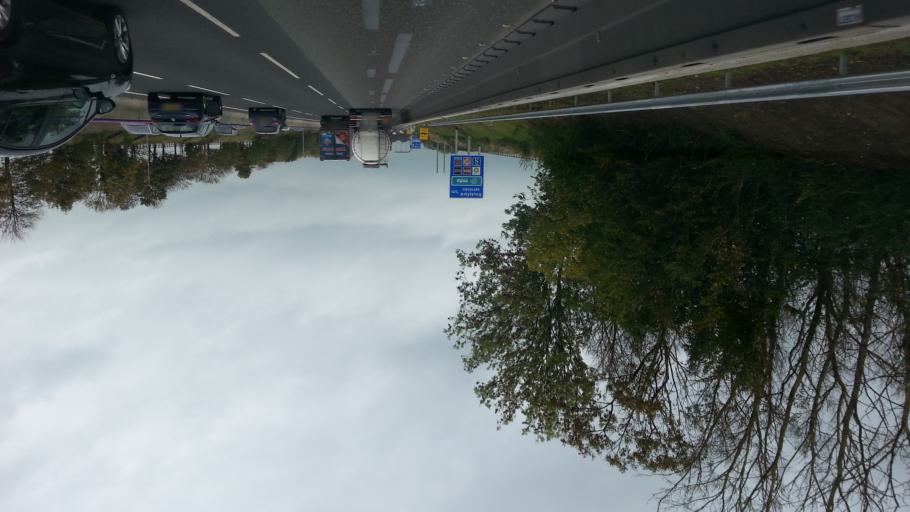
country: GB
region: England
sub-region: Cheshire East
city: Knutsford
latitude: 53.2903
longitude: -2.3960
